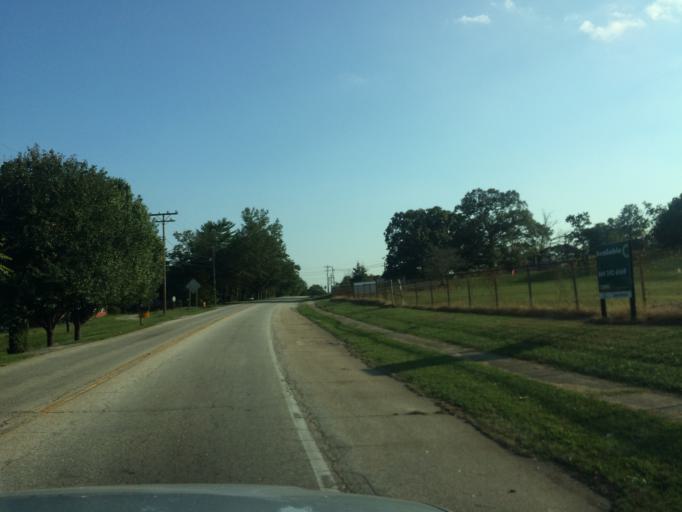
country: US
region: South Carolina
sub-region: Anderson County
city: Piedmont
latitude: 34.7052
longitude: -82.4536
